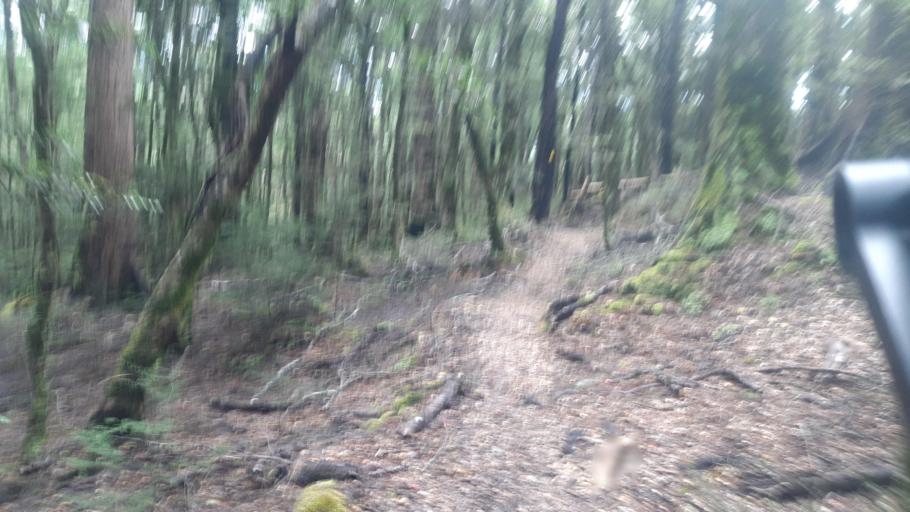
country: NZ
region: Tasman
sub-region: Tasman District
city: Wakefield
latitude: -41.7697
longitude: 172.8173
